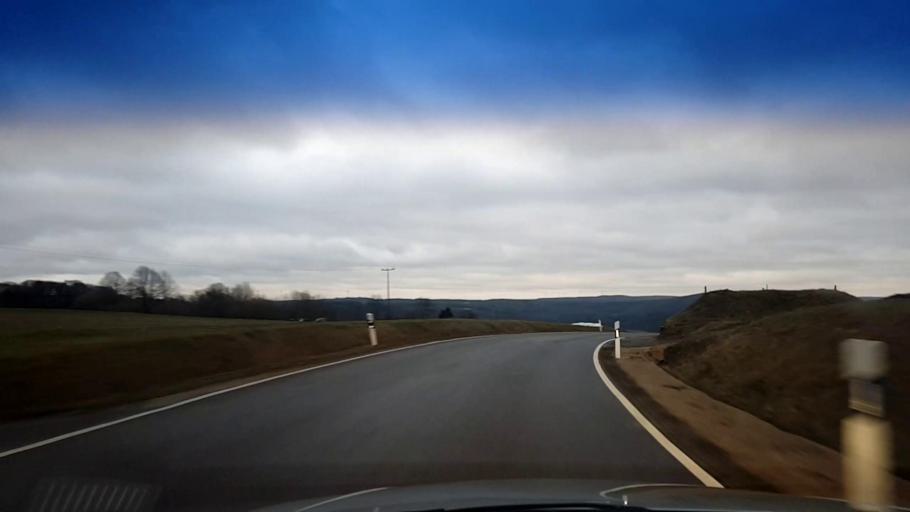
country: DE
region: Bavaria
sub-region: Upper Franconia
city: Wattendorf
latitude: 50.0272
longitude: 11.0663
